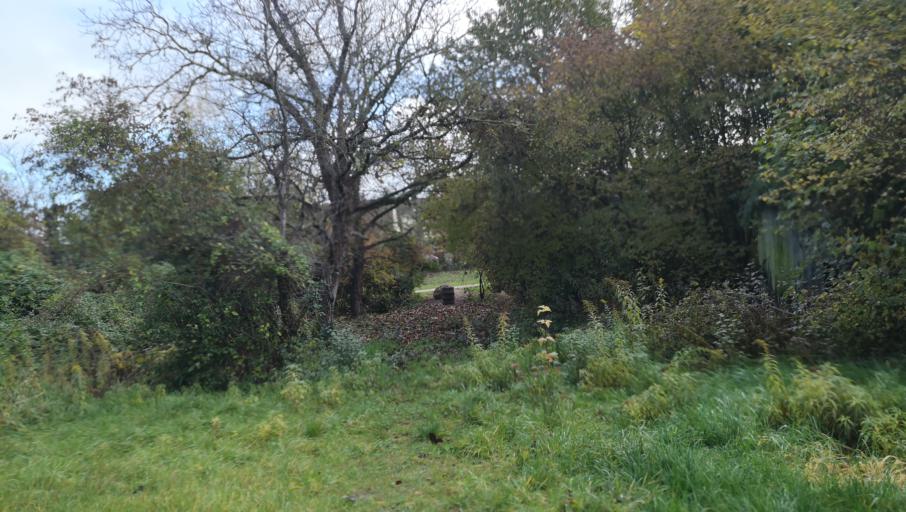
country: FR
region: Centre
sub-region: Departement du Loiret
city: Semoy
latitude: 47.9075
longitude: 1.9414
